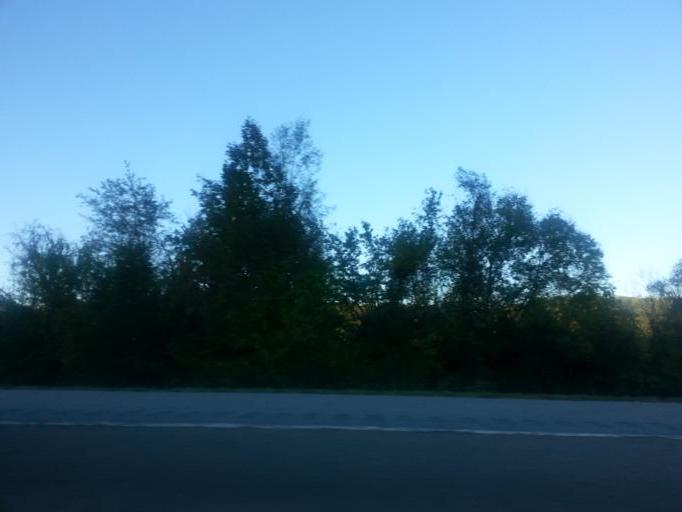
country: US
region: Tennessee
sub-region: Anderson County
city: Rocky Top
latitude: 36.2089
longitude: -84.1269
